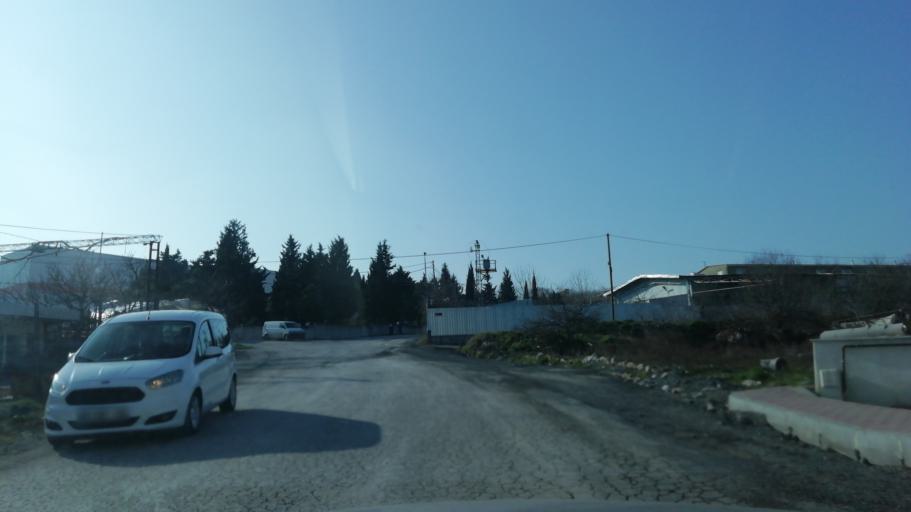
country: TR
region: Istanbul
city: Esenyurt
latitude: 41.1133
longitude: 28.6408
